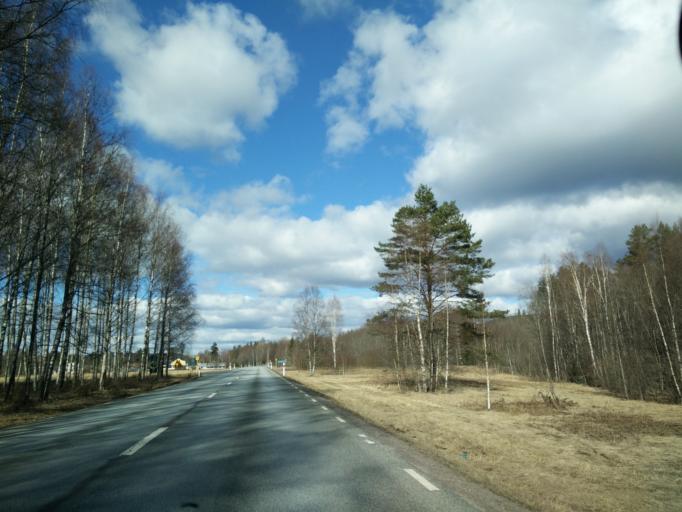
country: SE
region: Vaermland
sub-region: Munkfors Kommun
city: Munkfors
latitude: 59.8680
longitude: 13.5614
